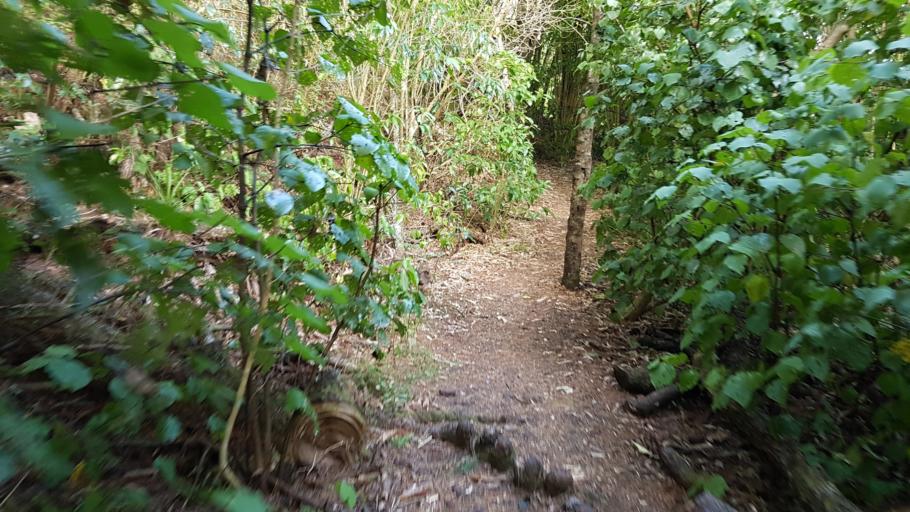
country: NZ
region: Auckland
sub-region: Auckland
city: North Shore
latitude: -36.8187
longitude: 174.7203
